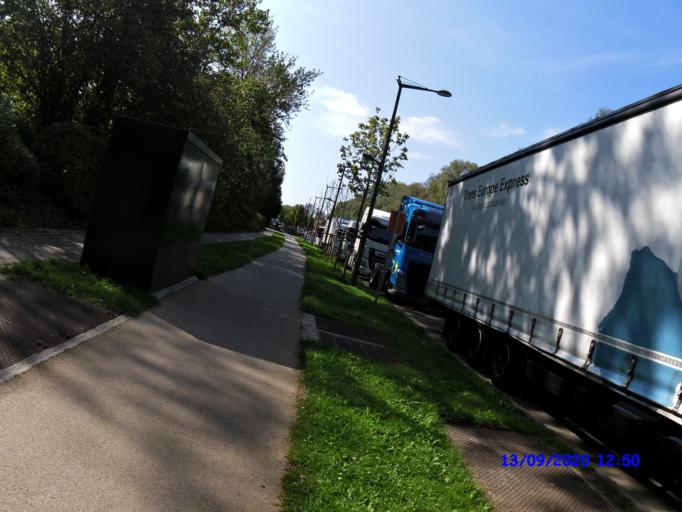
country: BE
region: Flanders
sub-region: Provincie Vlaams-Brabant
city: Dilbeek
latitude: 50.8689
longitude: 4.2840
